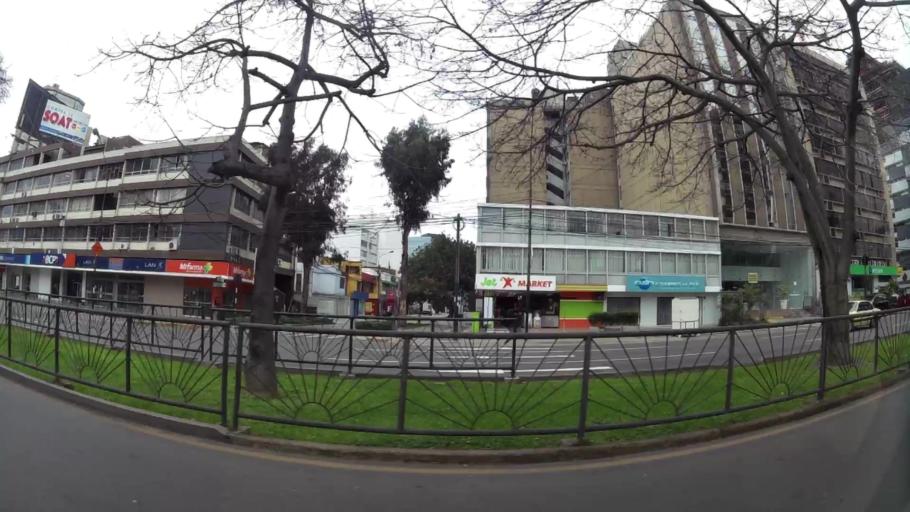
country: PE
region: Lima
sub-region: Lima
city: San Isidro
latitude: -12.0968
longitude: -77.0232
